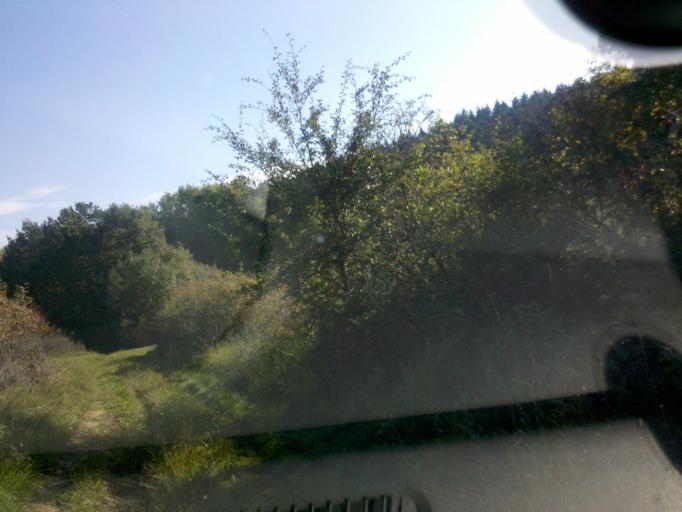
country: DE
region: Hesse
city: Herborn
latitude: 50.6864
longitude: 8.3331
